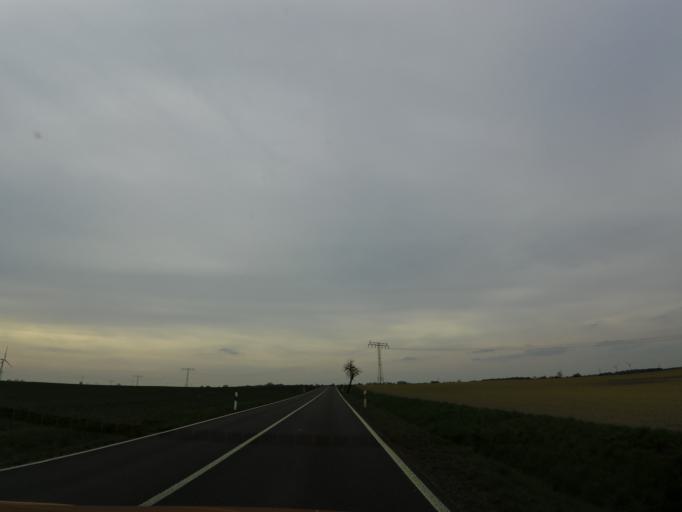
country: DE
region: Brandenburg
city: Tauche
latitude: 52.1772
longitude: 14.1792
